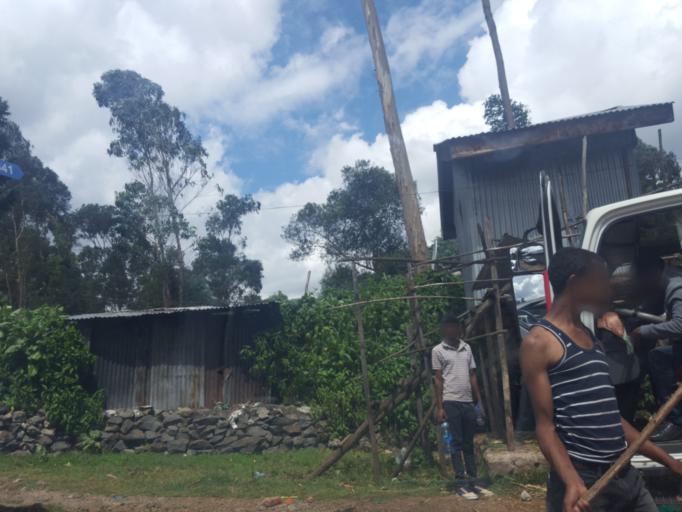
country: ET
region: Adis Abeba
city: Addis Ababa
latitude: 9.0632
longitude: 38.7655
